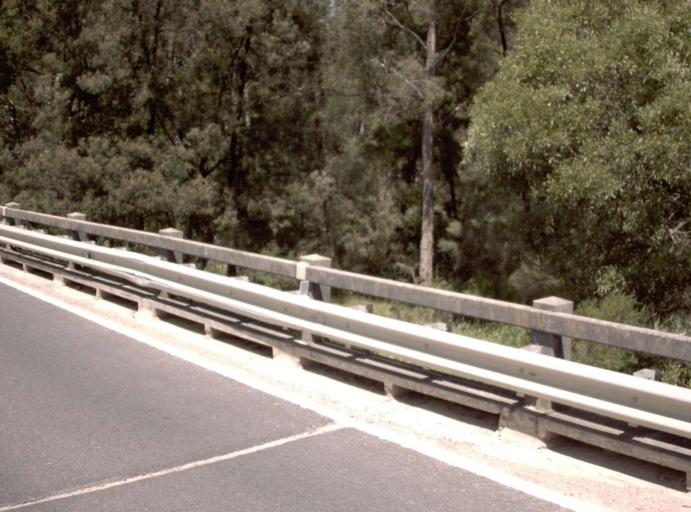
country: AU
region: New South Wales
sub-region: Bombala
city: Bombala
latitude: -37.5706
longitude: 149.1362
